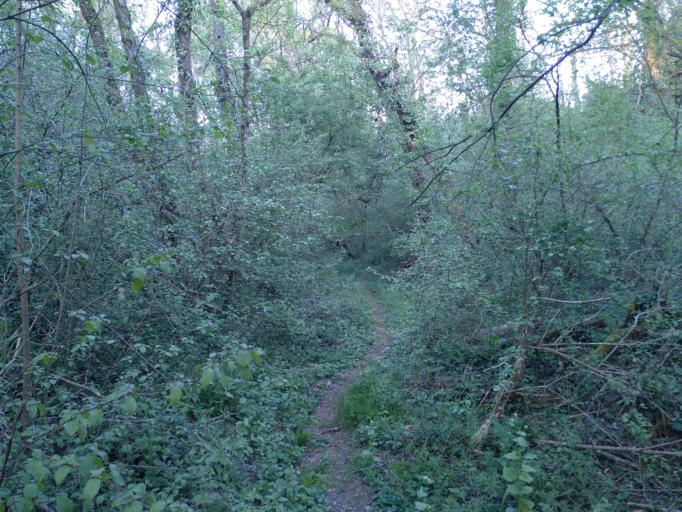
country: FR
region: Rhone-Alpes
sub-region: Departement du Rhone
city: Vernaison
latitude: 45.6396
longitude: 4.8166
